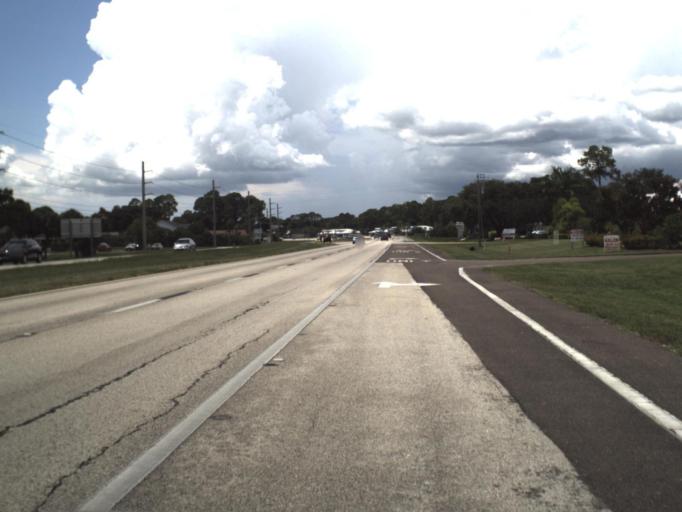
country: US
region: Florida
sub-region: Charlotte County
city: Port Charlotte
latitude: 27.0162
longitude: -82.1531
